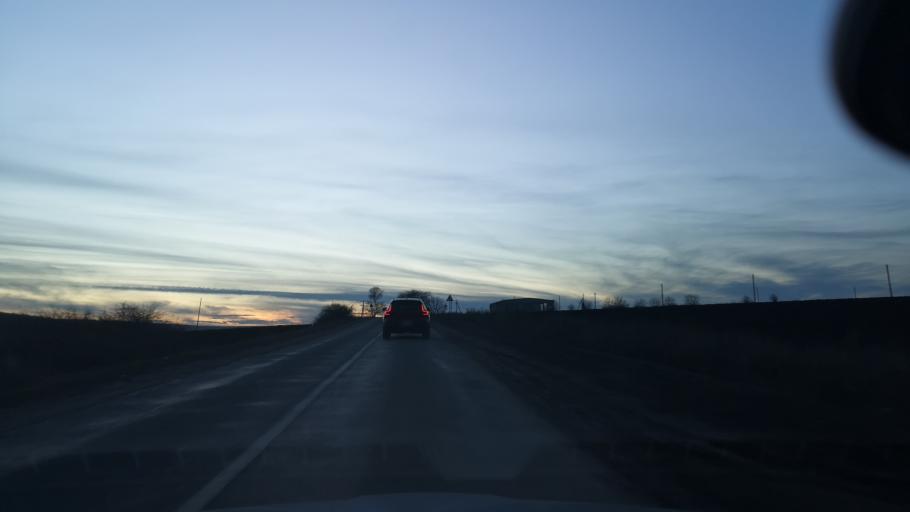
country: MD
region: Orhei
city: Orhei
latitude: 47.2997
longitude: 28.9142
